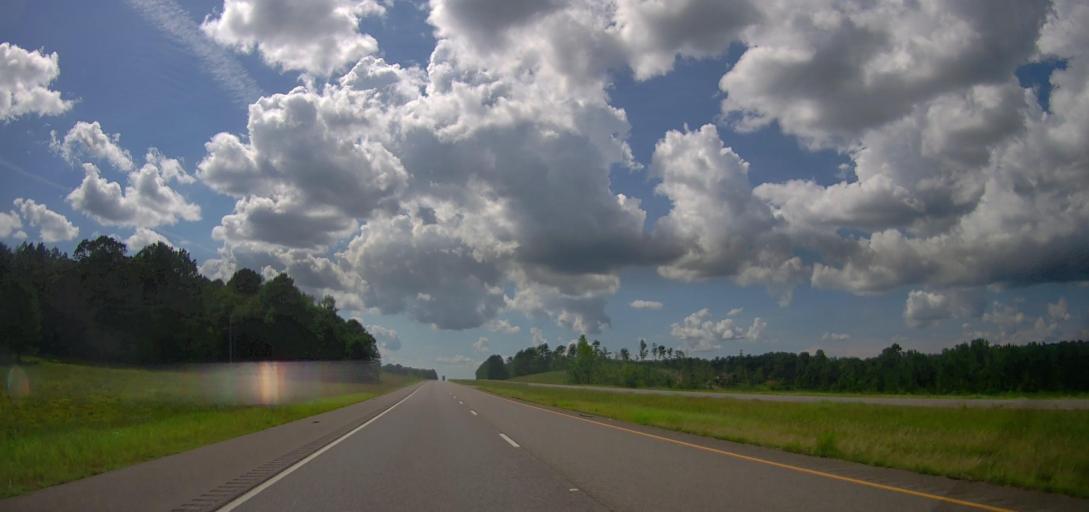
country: US
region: Alabama
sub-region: Pickens County
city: Reform
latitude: 33.3930
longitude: -88.0485
